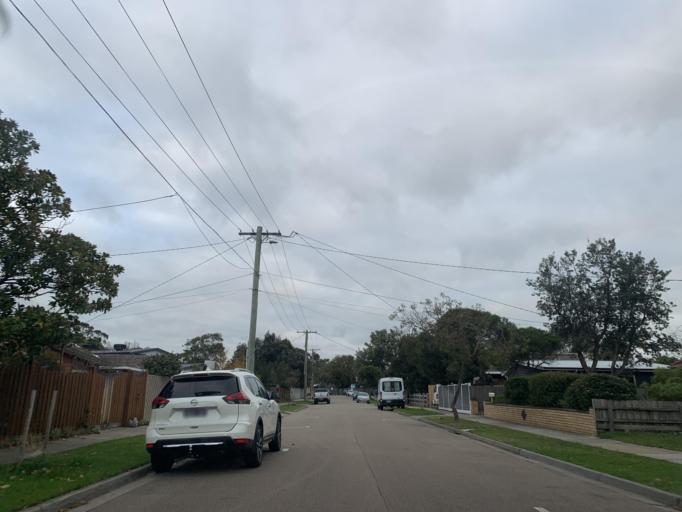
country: AU
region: Victoria
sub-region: Frankston
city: Seaford
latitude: -38.0922
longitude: 145.1320
